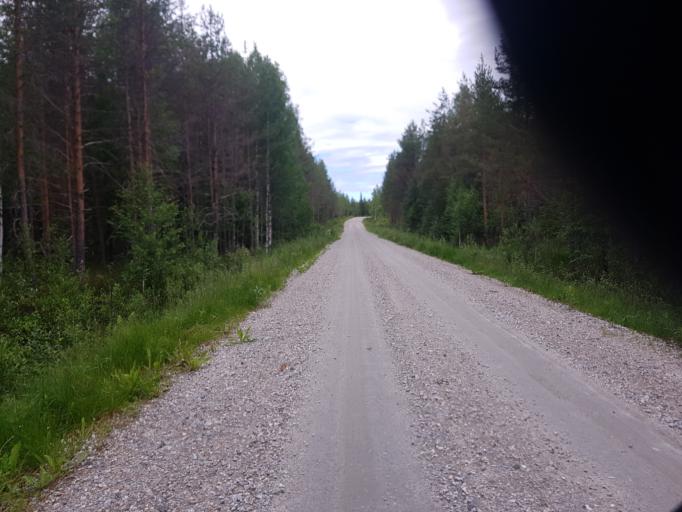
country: FI
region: Kainuu
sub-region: Kehys-Kainuu
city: Kuhmo
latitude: 64.4319
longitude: 29.5807
